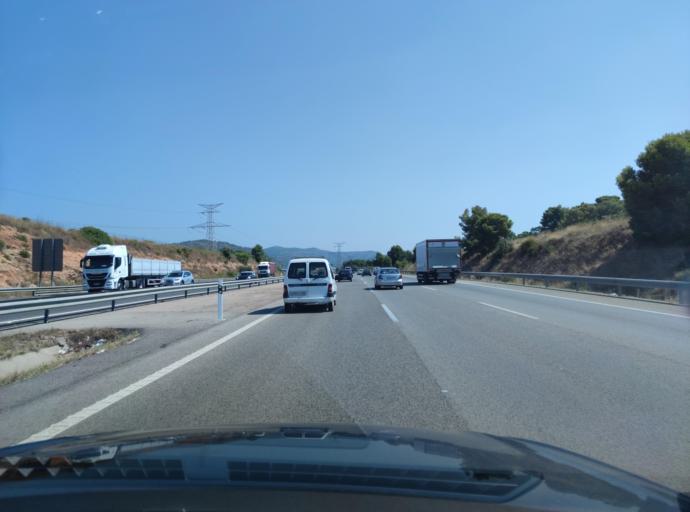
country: ES
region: Valencia
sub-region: Provincia de Valencia
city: Petres
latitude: 39.6654
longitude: -0.3033
